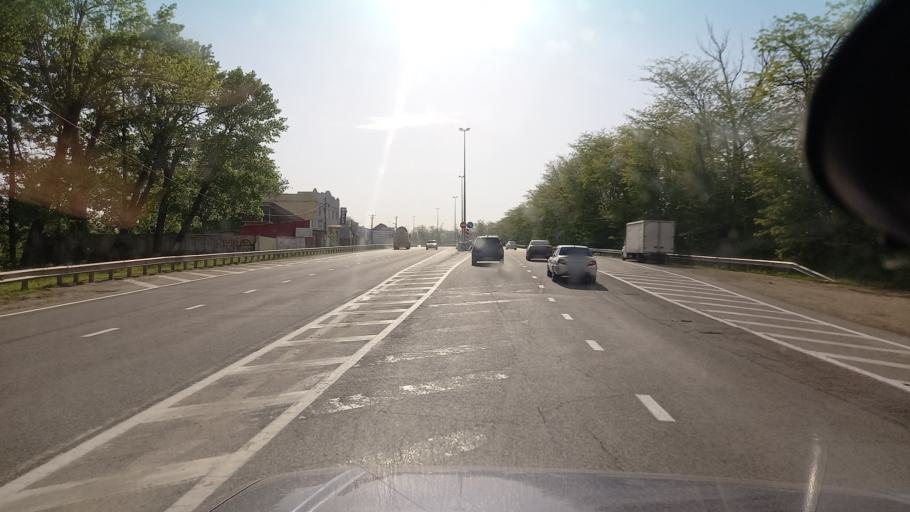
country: RU
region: Krasnodarskiy
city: Yelizavetinskaya
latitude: 45.0568
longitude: 38.8717
